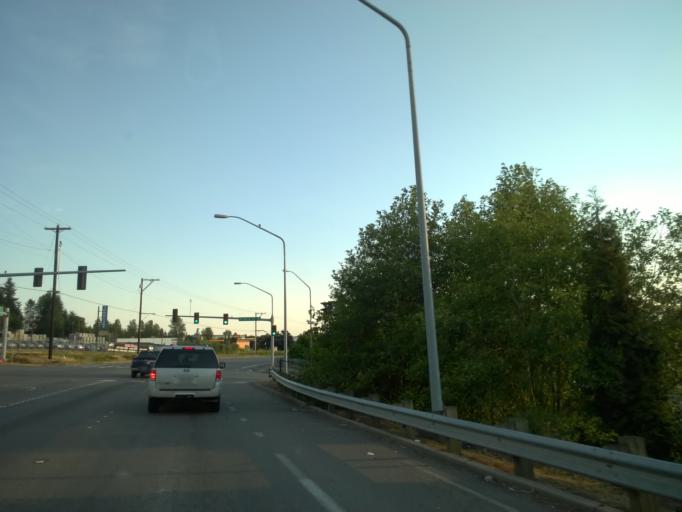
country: US
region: Washington
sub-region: King County
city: Woodinville
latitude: 47.7796
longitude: -122.1465
